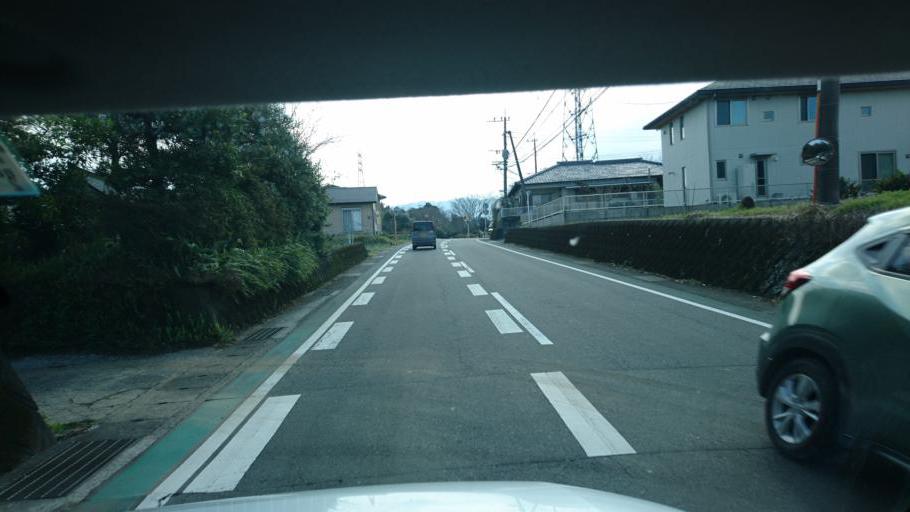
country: JP
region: Miyazaki
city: Miyazaki-shi
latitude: 31.8389
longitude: 131.3934
